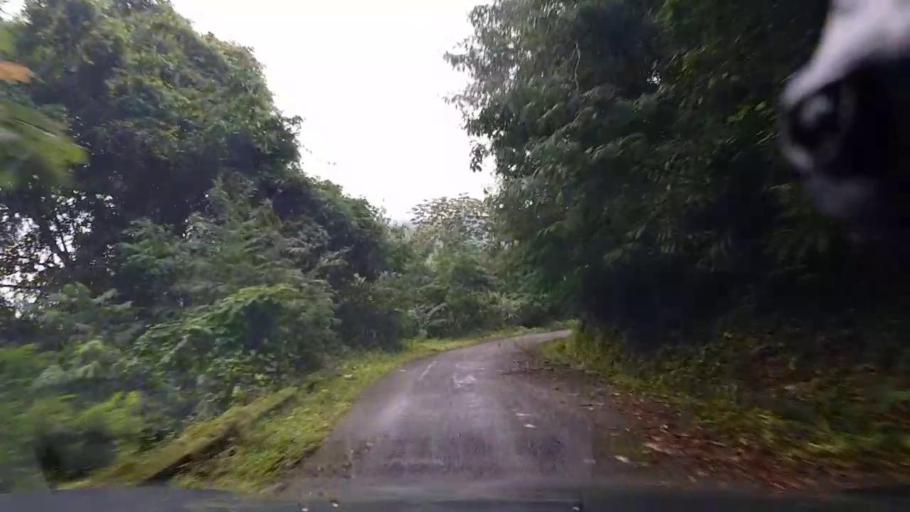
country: JM
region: Saint Andrew
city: Gordon Town
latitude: 18.1052
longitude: -76.7168
